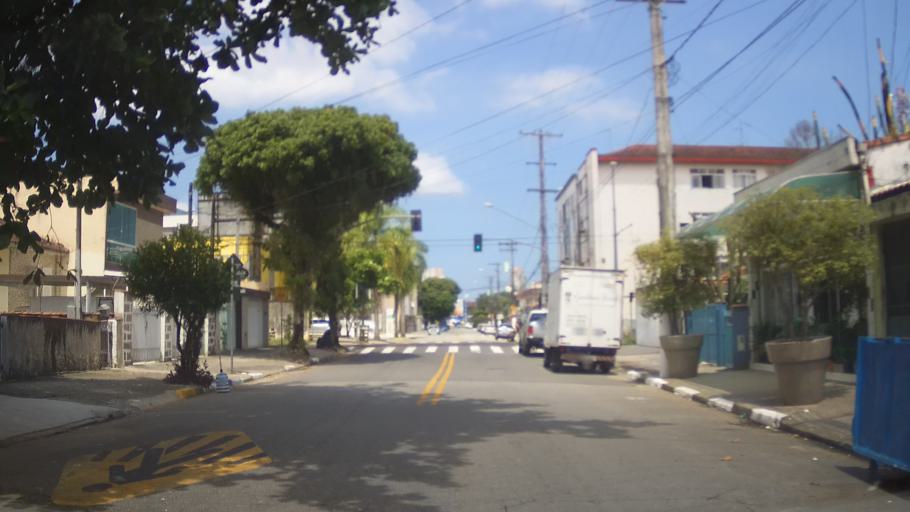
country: BR
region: Sao Paulo
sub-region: Santos
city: Santos
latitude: -23.9575
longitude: -46.3188
